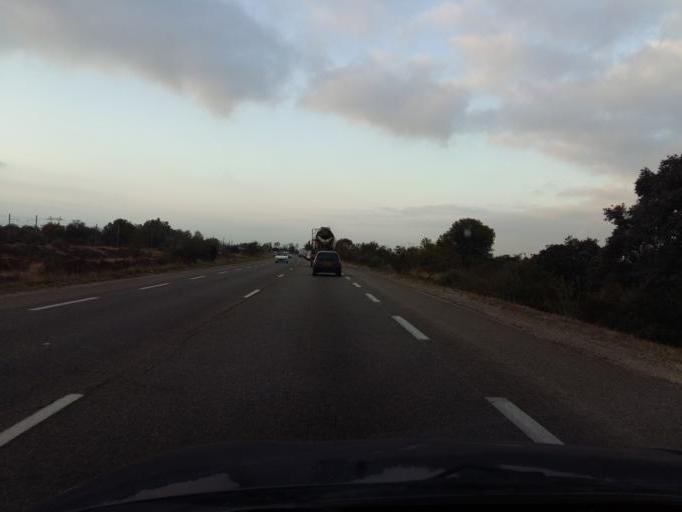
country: FR
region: Provence-Alpes-Cote d'Azur
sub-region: Departement des Bouches-du-Rhone
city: Istres
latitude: 43.5534
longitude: 4.9595
